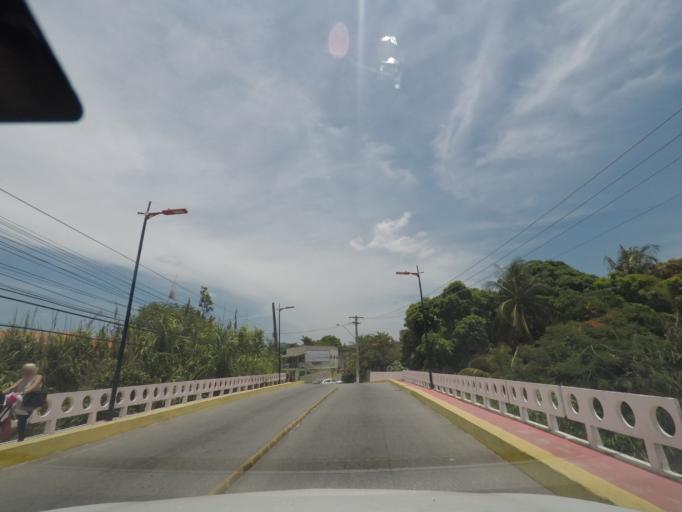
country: BR
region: Rio de Janeiro
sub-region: Marica
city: Marica
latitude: -22.9133
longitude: -42.8203
